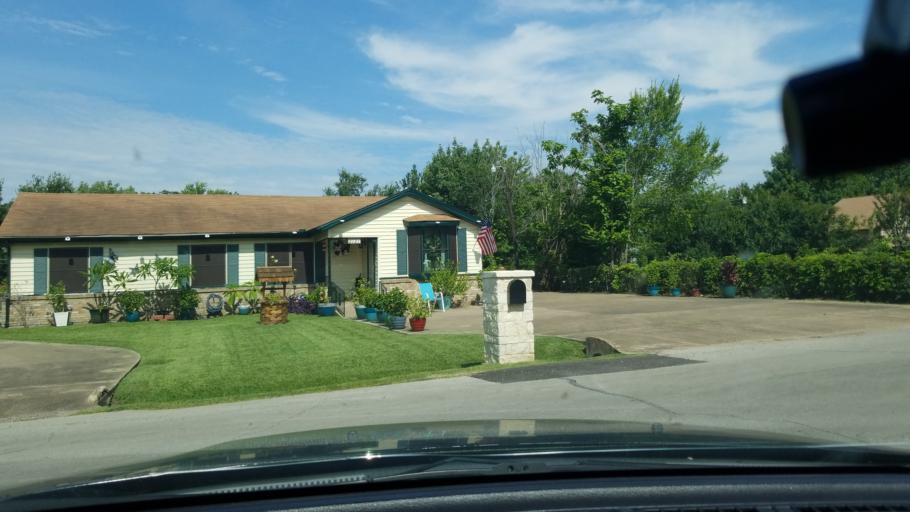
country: US
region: Texas
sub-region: Dallas County
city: Balch Springs
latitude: 32.7319
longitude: -96.6263
